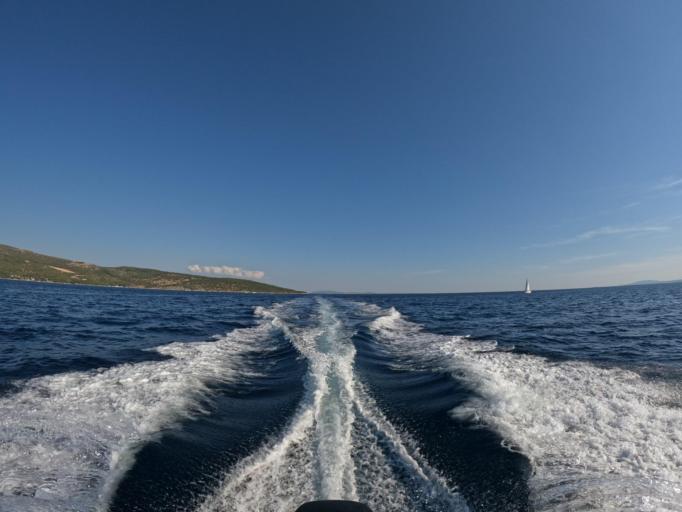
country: HR
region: Primorsko-Goranska
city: Punat
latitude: 44.9967
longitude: 14.6010
